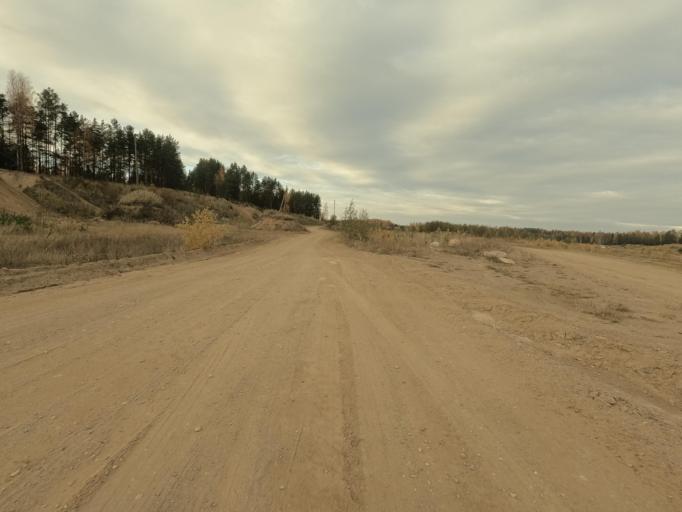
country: RU
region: Leningrad
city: Priladozhskiy
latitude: 59.7069
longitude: 31.3643
